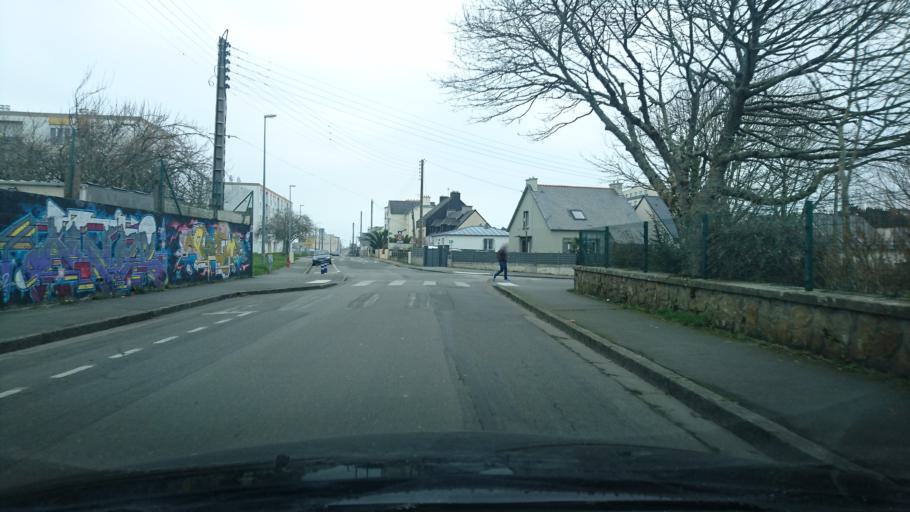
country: FR
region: Brittany
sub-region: Departement du Finistere
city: Brest
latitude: 48.3853
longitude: -4.5251
